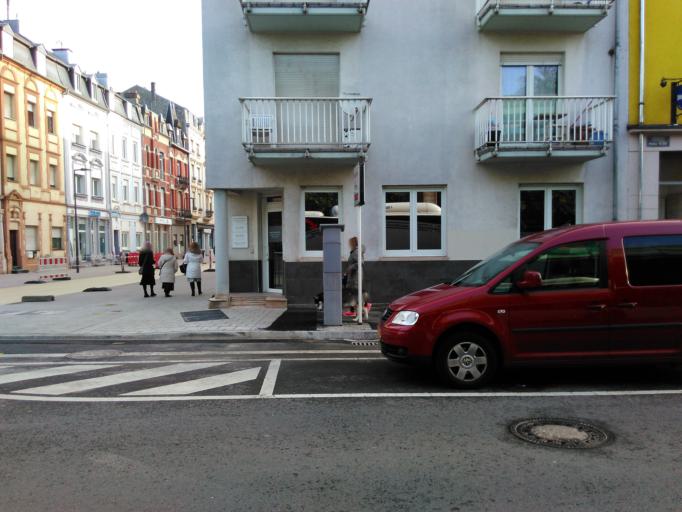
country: LU
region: Luxembourg
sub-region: Canton d'Esch-sur-Alzette
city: Esch-sur-Alzette
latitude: 49.4916
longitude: 5.9749
